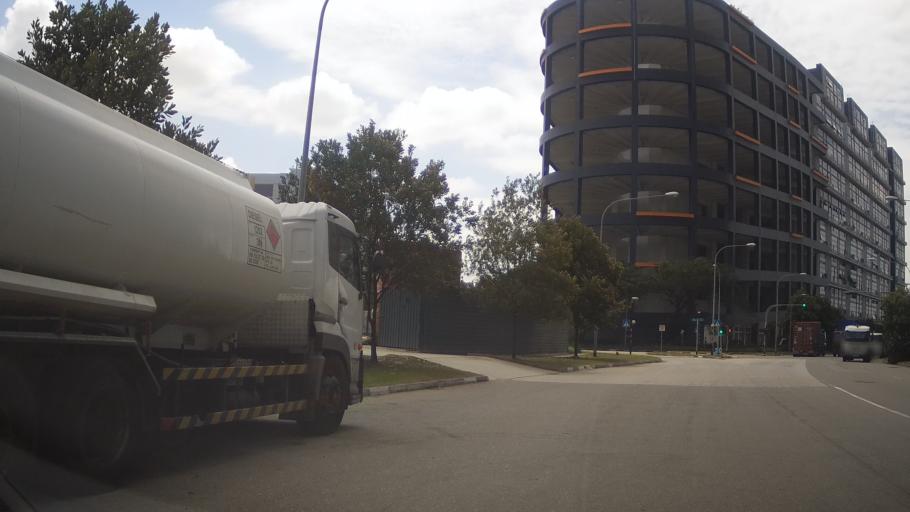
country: SG
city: Singapore
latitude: 1.3124
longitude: 103.6981
